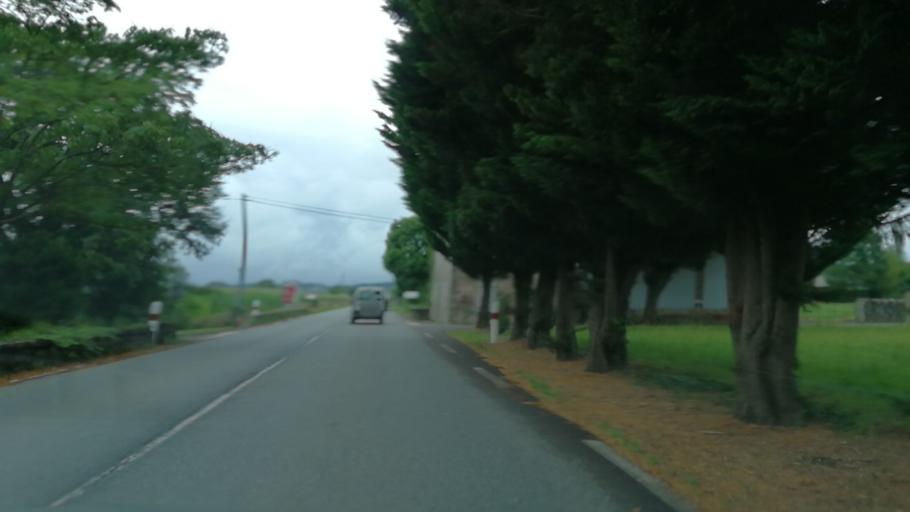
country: FR
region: Aquitaine
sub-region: Departement des Pyrenees-Atlantiques
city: Oloron-Sainte-Marie
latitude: 43.1424
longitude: -0.6030
